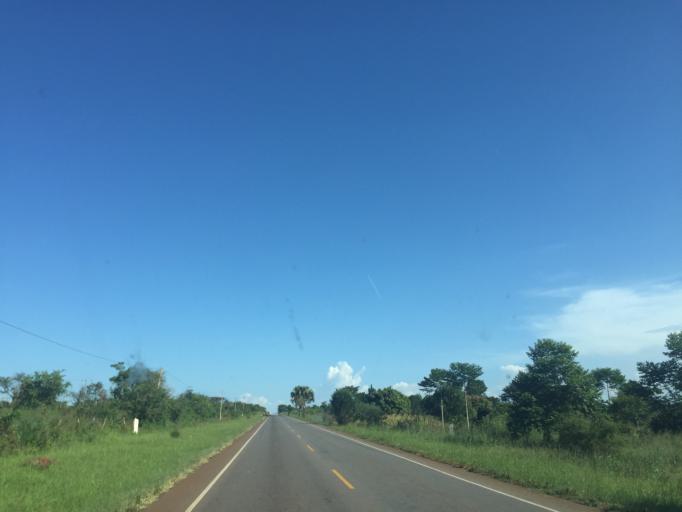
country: UG
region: Central Region
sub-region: Nakasongola District
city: Nakasongola
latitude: 1.3465
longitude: 32.3887
